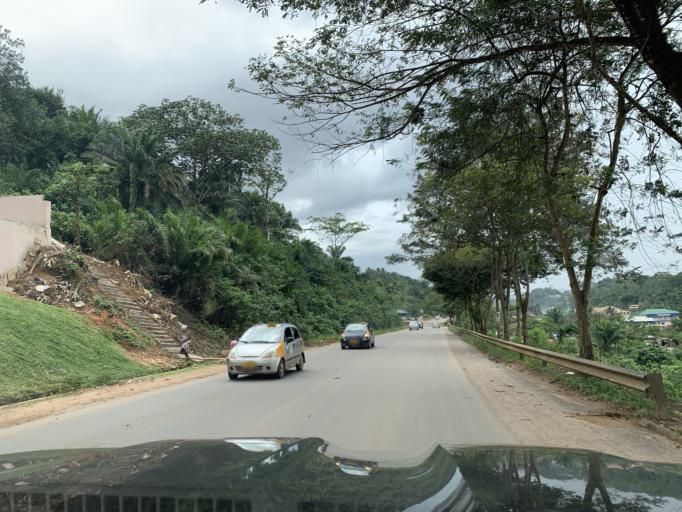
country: GH
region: Western
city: Tarkwa
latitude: 5.3237
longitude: -1.9836
